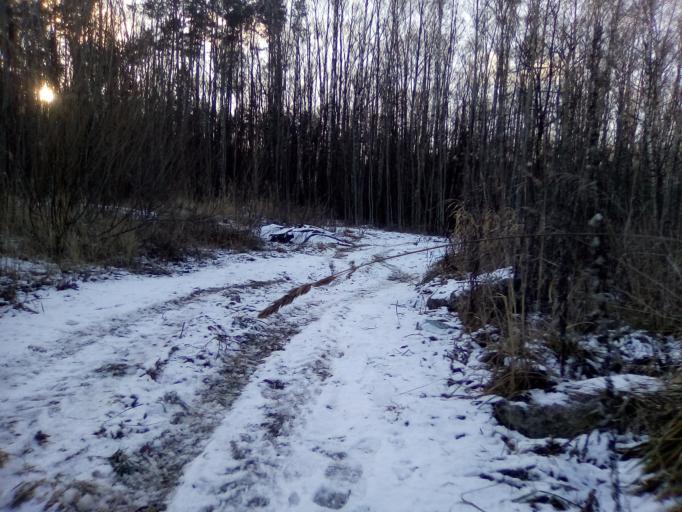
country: RU
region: Moskovskaya
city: Lesnoy Gorodok
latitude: 55.6490
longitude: 37.1795
